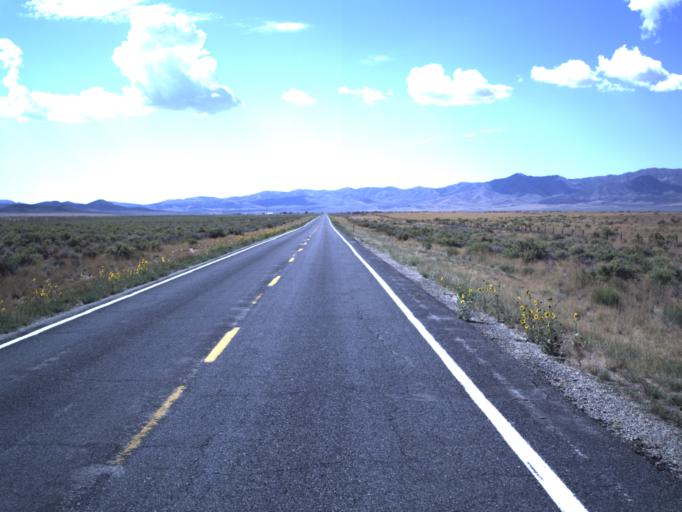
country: US
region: Utah
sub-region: Tooele County
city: Tooele
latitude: 40.1367
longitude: -112.4308
